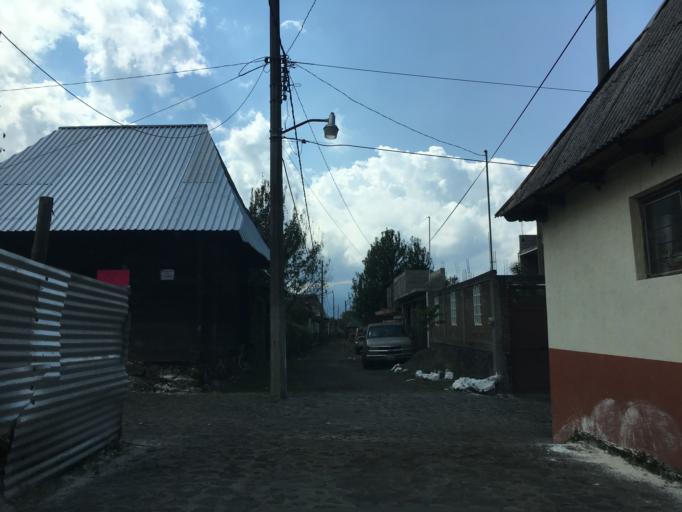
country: MX
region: Michoacan
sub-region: Uruapan
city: Santa Ana Zirosto
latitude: 19.5651
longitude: -102.2856
